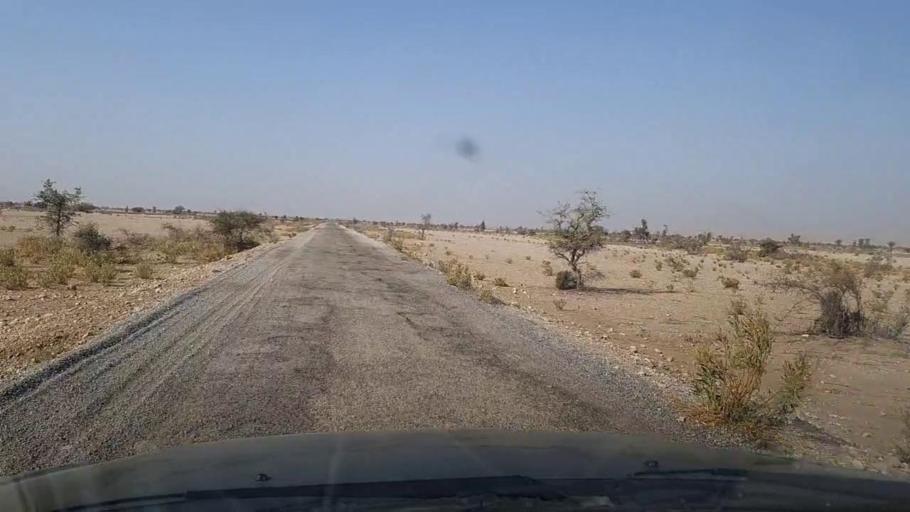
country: PK
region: Sindh
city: Sann
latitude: 25.9175
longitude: 68.0128
